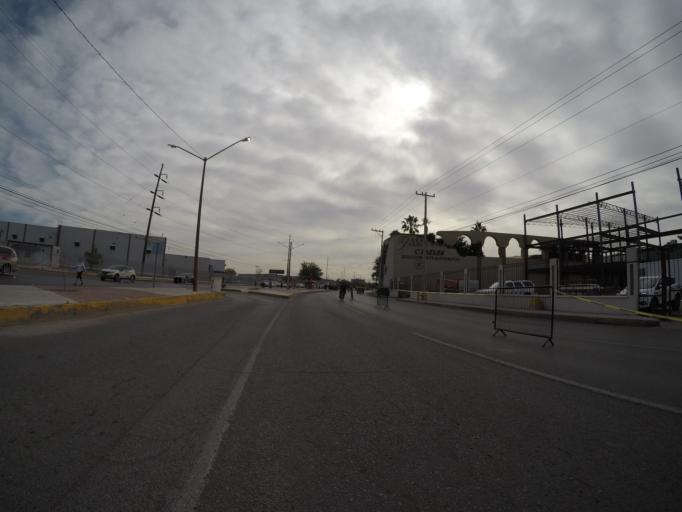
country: MX
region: Chihuahua
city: Ciudad Juarez
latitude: 31.7238
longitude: -106.4008
